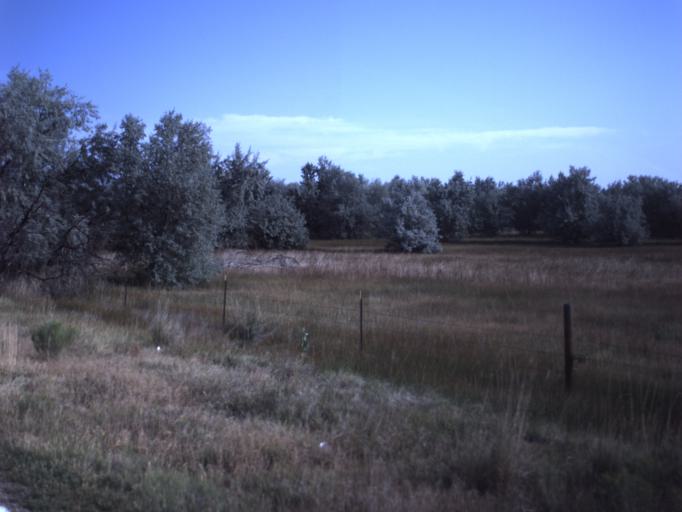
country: US
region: Utah
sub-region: Duchesne County
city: Duchesne
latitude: 40.3208
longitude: -110.2589
